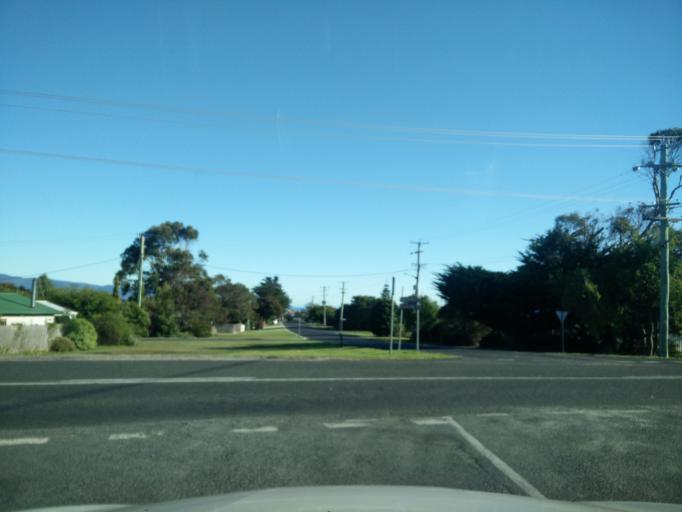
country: AU
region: Tasmania
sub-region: Break O'Day
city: St Helens
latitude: -41.8697
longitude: 148.2898
